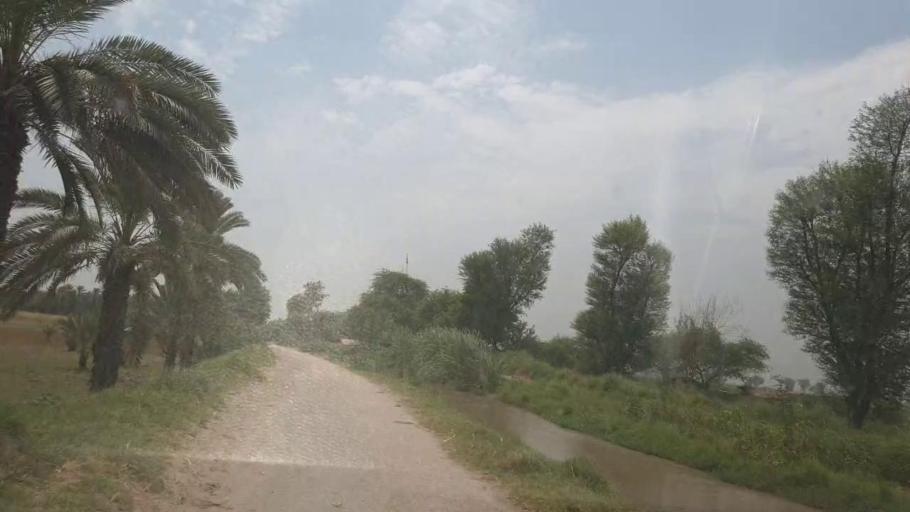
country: PK
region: Sindh
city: Kot Diji
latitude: 27.4446
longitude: 68.6772
